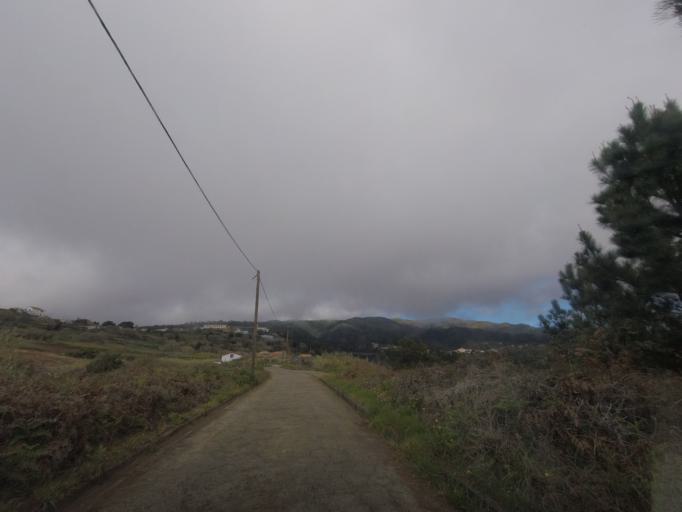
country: PT
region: Madeira
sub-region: Calheta
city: Faja da Ovelha
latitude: 32.7610
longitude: -17.2182
